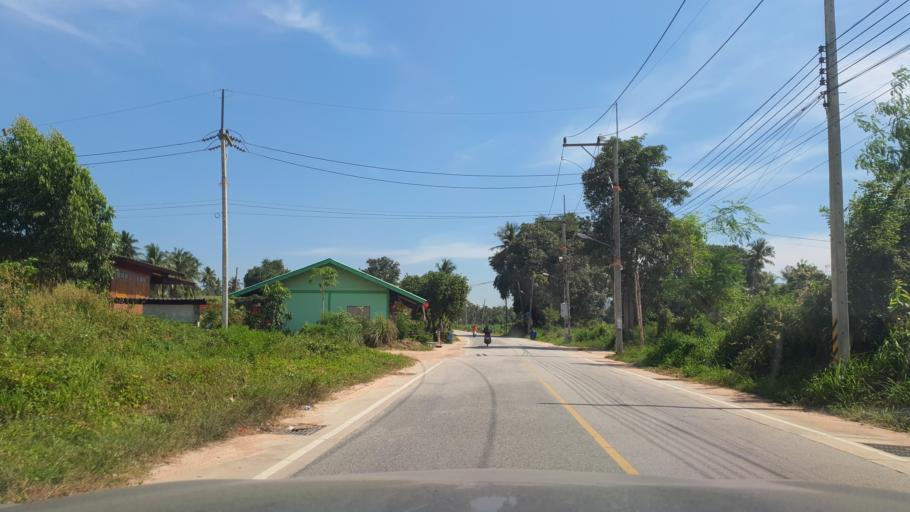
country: TH
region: Chon Buri
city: Bang Lamung
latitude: 12.9842
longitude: 100.9767
